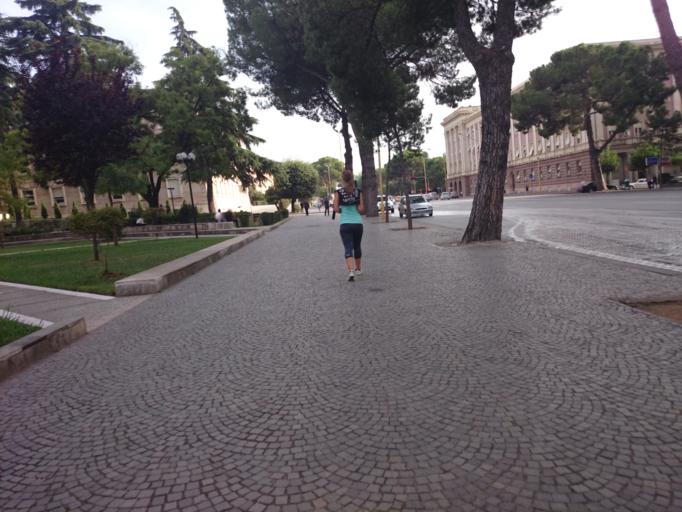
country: AL
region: Tirane
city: Tirana
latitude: 41.3227
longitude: 19.8202
